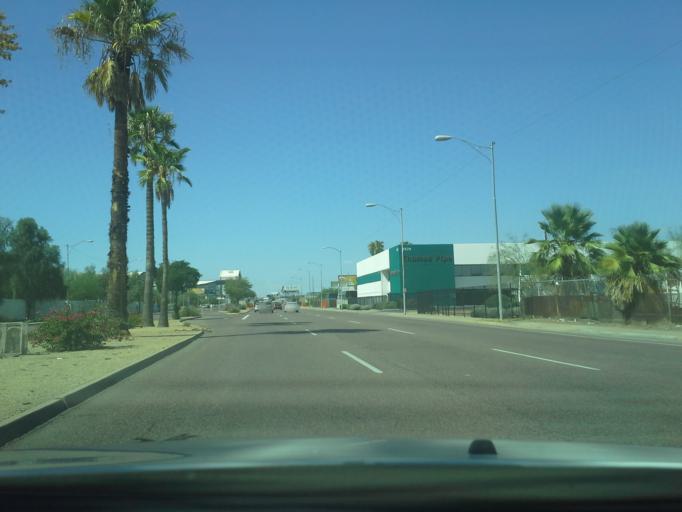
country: US
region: Arizona
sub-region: Maricopa County
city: Phoenix
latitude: 33.4335
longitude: -112.0651
